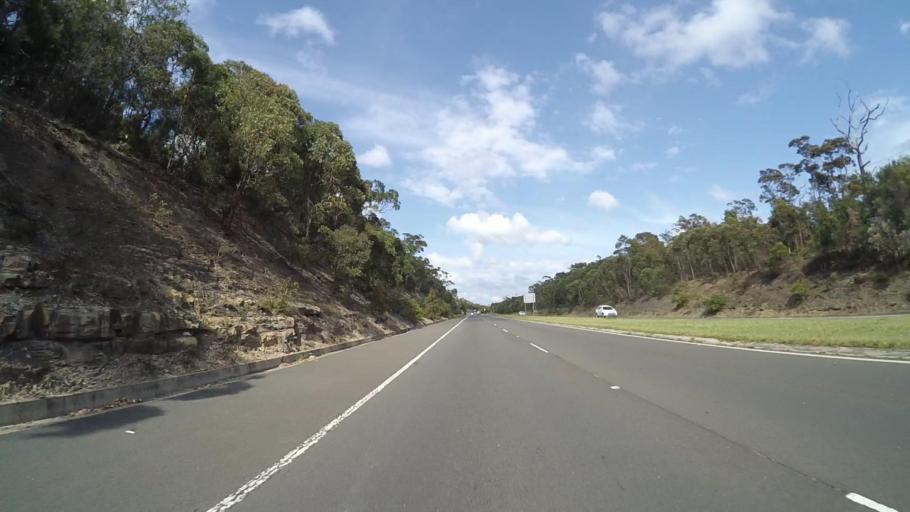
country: AU
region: New South Wales
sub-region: Sutherland Shire
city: Loftus
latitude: -34.0551
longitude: 151.0441
